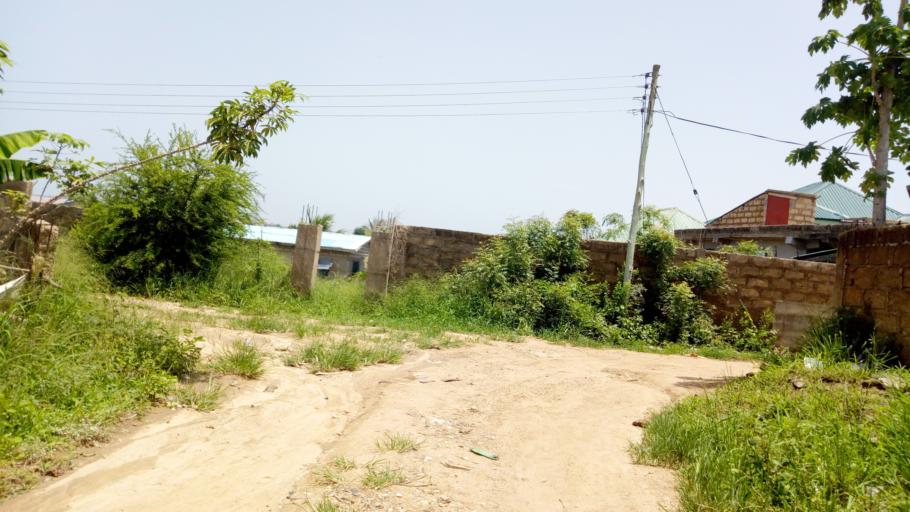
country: GH
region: Central
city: Kasoa
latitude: 5.5025
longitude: -0.4536
